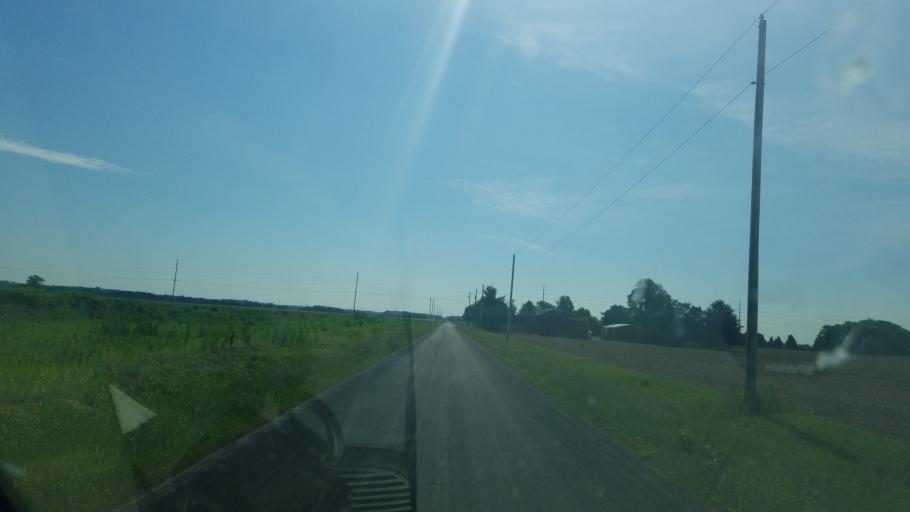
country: US
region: Ohio
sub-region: Wyandot County
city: Carey
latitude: 40.9781
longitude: -83.3084
